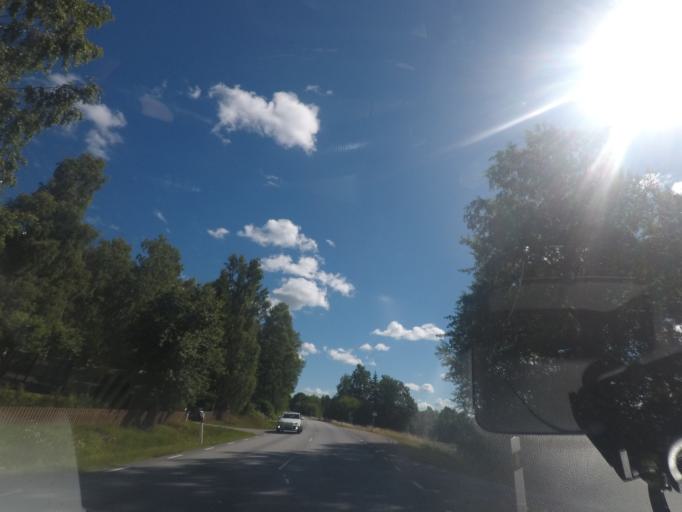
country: SE
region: Stockholm
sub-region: Norrtalje Kommun
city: Skanninge
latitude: 59.8939
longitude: 18.4585
